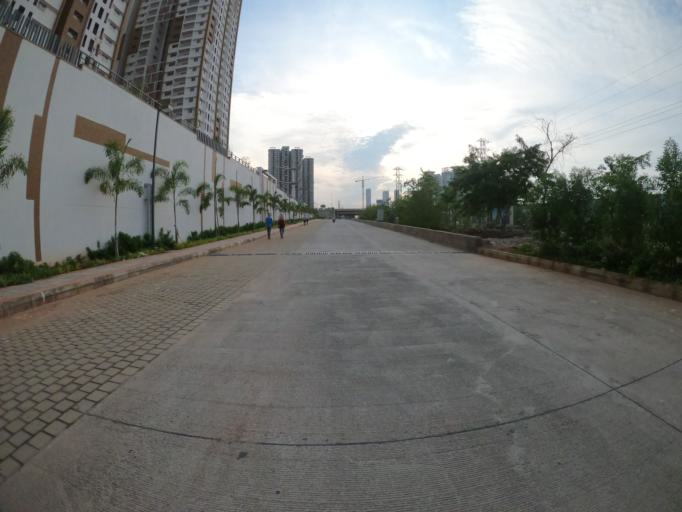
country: IN
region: Telangana
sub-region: Hyderabad
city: Hyderabad
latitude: 17.4001
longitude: 78.3544
